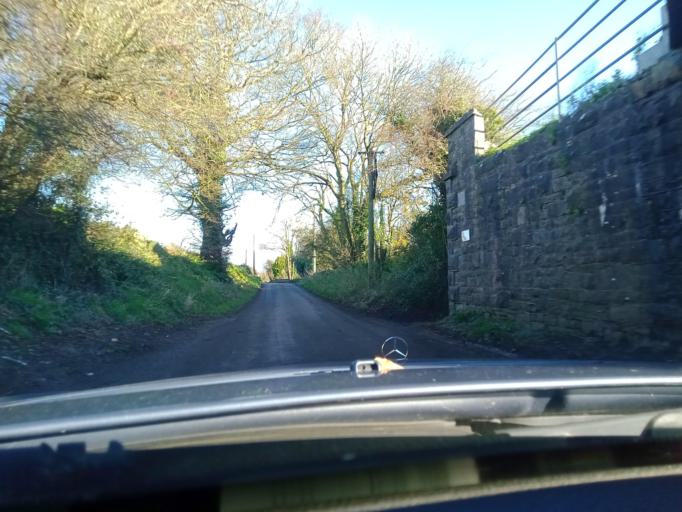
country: IE
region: Leinster
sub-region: Kilkenny
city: Mooncoin
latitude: 52.3004
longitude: -7.2050
